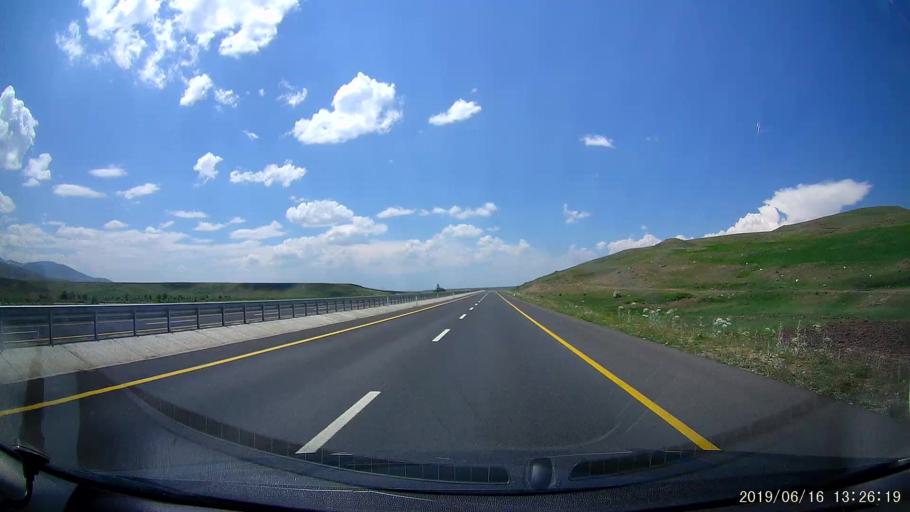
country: TR
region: Agri
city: Taslicay
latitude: 39.6583
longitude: 43.3310
